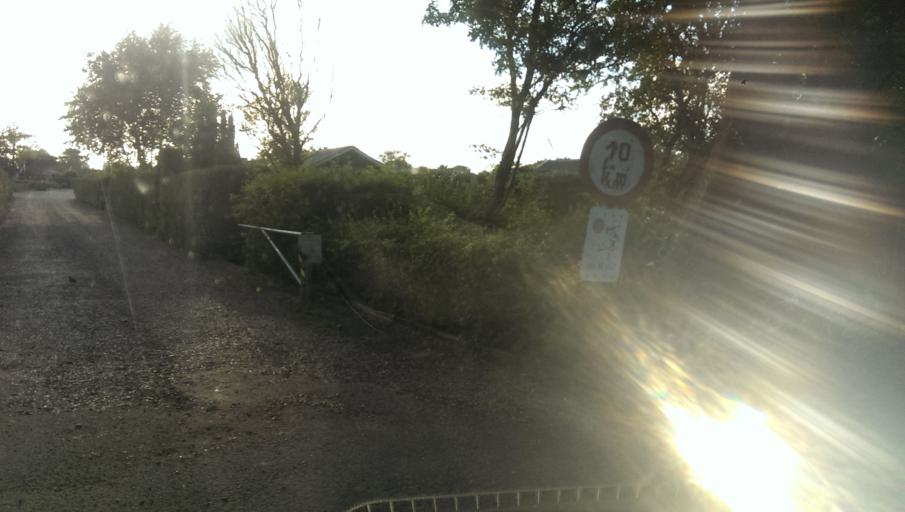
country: DK
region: South Denmark
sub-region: Esbjerg Kommune
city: Esbjerg
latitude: 55.5256
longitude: 8.4966
